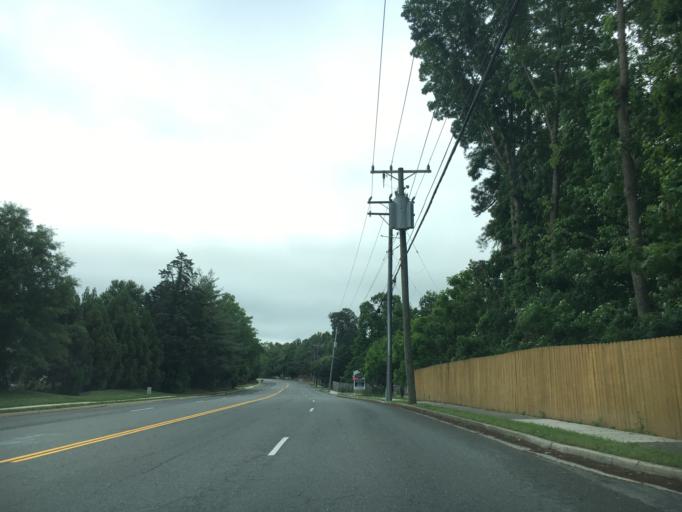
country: US
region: Virginia
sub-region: Henrico County
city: Short Pump
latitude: 37.6324
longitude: -77.6240
